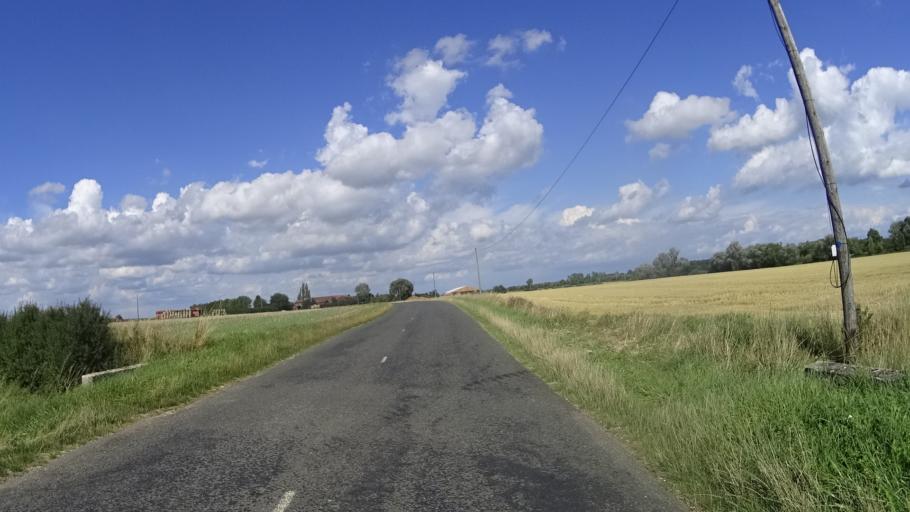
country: FR
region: Champagne-Ardenne
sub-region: Departement de la Marne
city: Pargny-sur-Saulx
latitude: 48.7399
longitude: 4.7874
